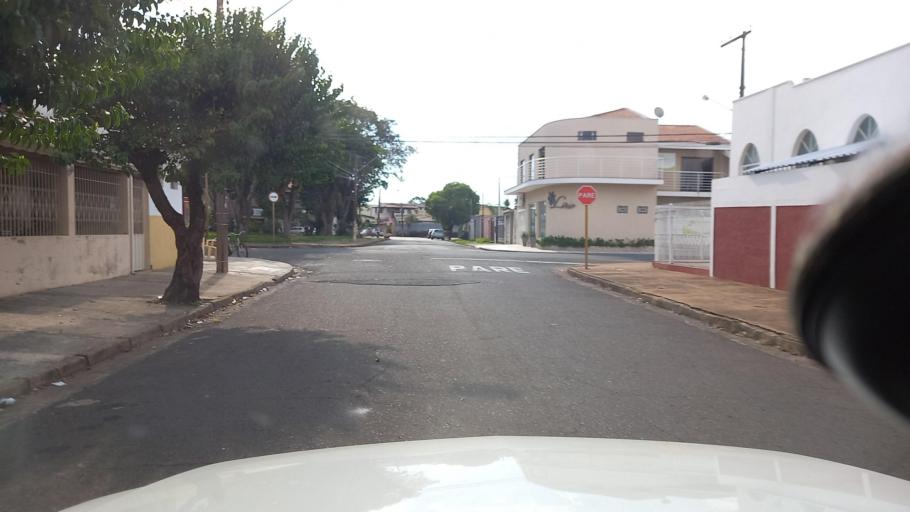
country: BR
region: Sao Paulo
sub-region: Moji-Guacu
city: Mogi-Gaucu
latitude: -22.3489
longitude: -46.9446
